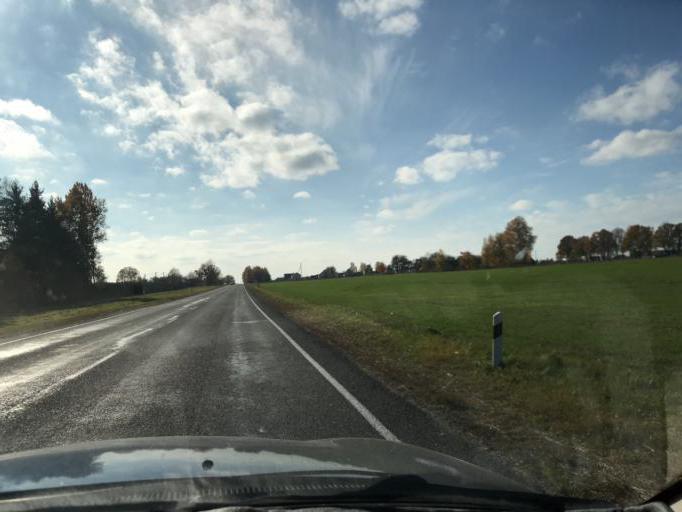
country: BY
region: Grodnenskaya
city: Voranava
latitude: 54.1721
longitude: 25.3327
